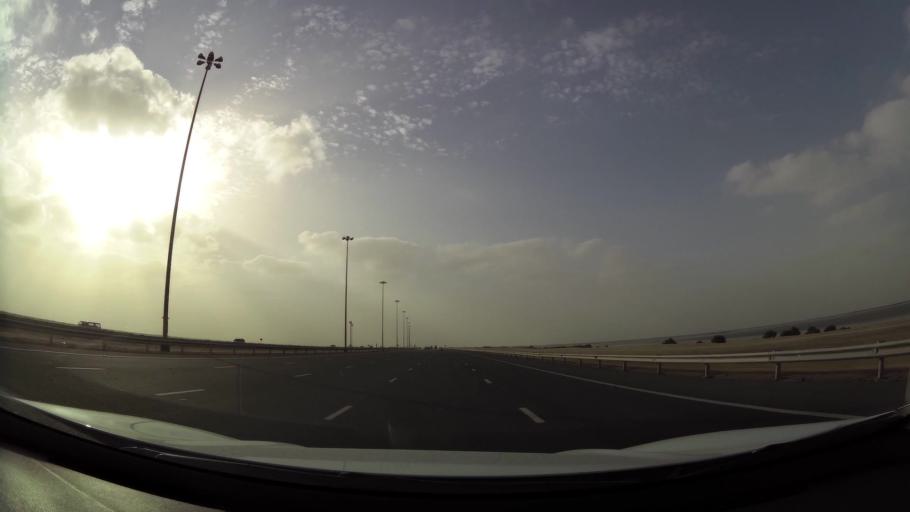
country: AE
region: Abu Dhabi
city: Abu Dhabi
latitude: 24.5143
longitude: 54.5420
